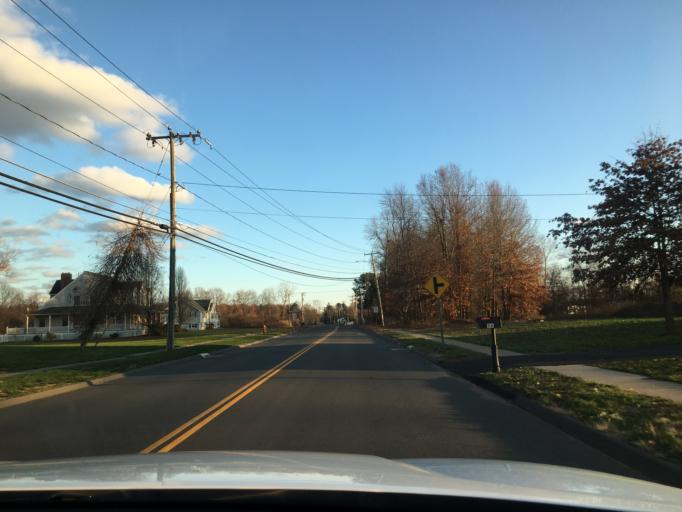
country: US
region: Connecticut
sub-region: Hartford County
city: Southwood Acres
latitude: 41.9643
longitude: -72.5806
